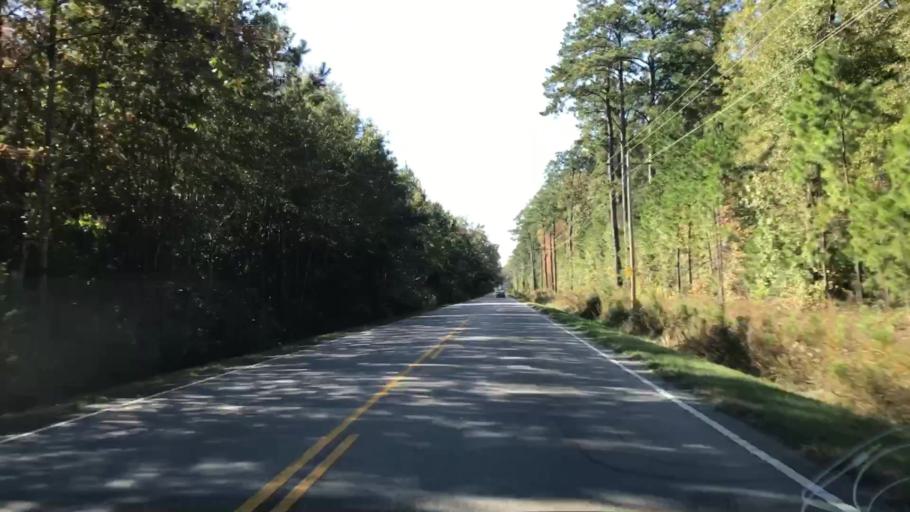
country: US
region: South Carolina
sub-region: Jasper County
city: Ridgeland
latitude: 32.4698
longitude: -80.8862
